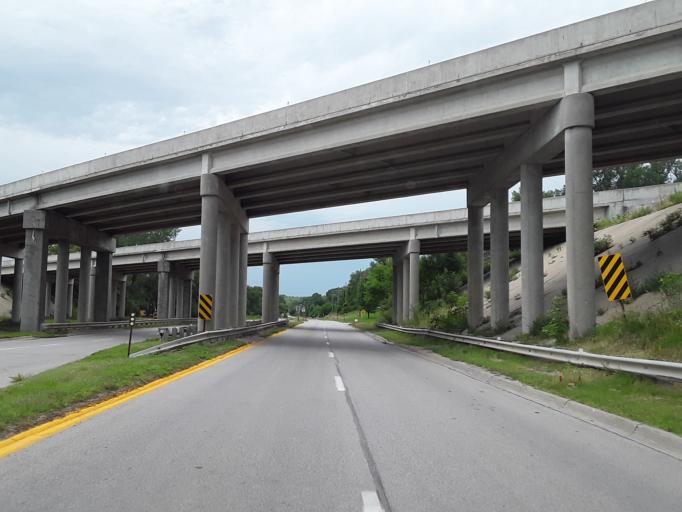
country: US
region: Iowa
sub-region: Pottawattamie County
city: Carter Lake
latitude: 41.3465
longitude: -95.9927
